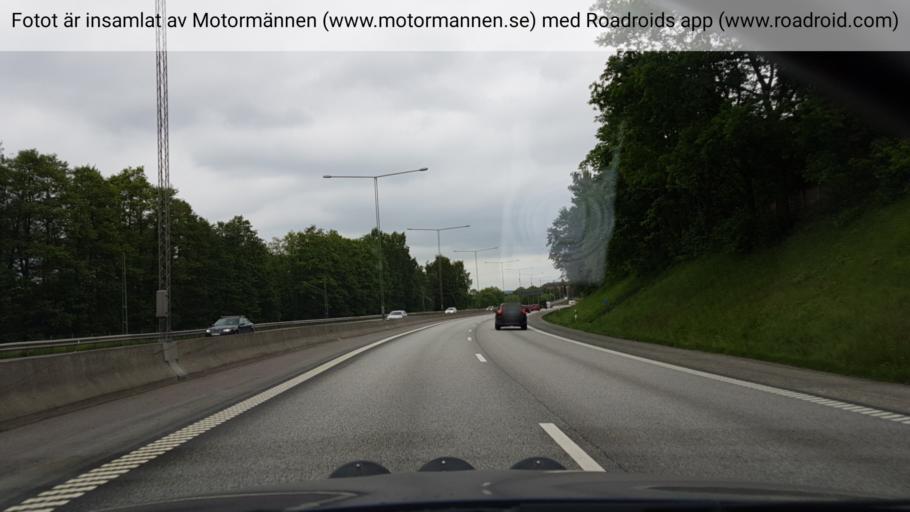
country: SE
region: Joenkoeping
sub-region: Jonkopings Kommun
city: Jonkoping
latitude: 57.7709
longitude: 14.1910
